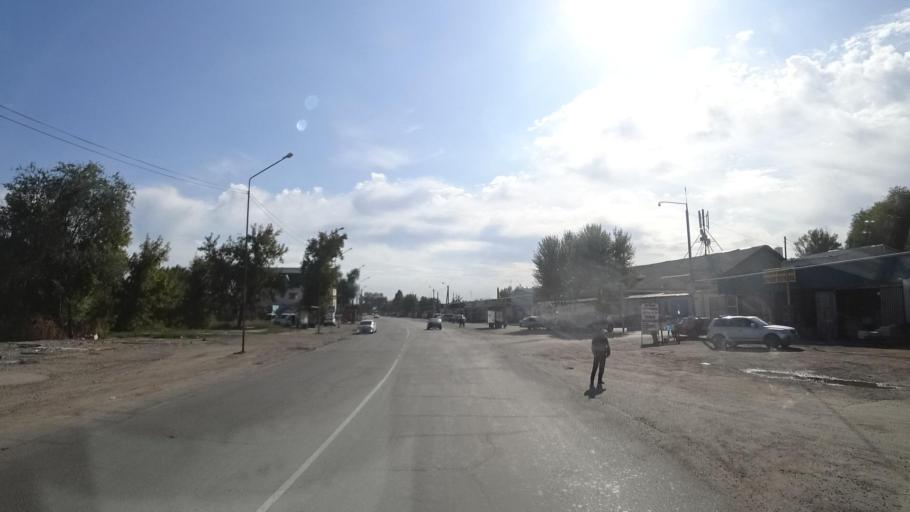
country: KZ
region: Almaty Oblysy
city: Energeticheskiy
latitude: 43.4056
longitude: 77.0123
